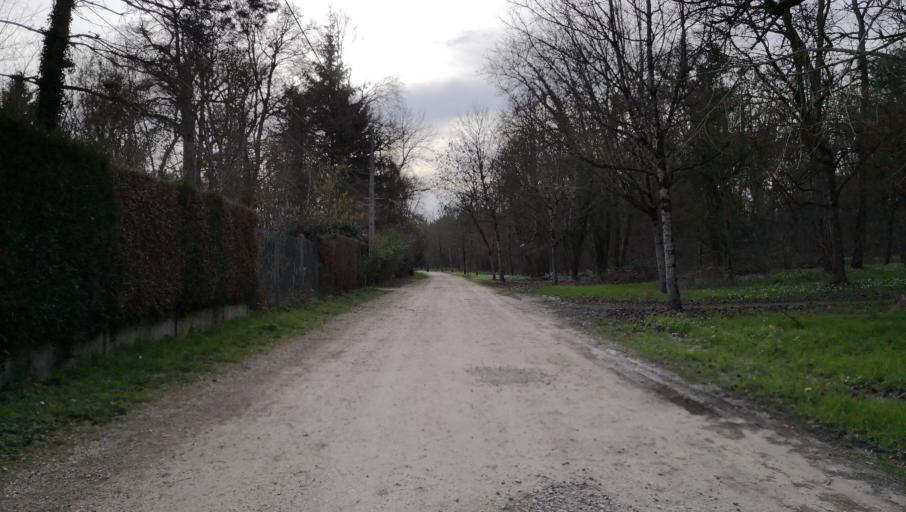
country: FR
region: Centre
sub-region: Departement du Loiret
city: La Chapelle-Saint-Mesmin
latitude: 47.8815
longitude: 1.8326
